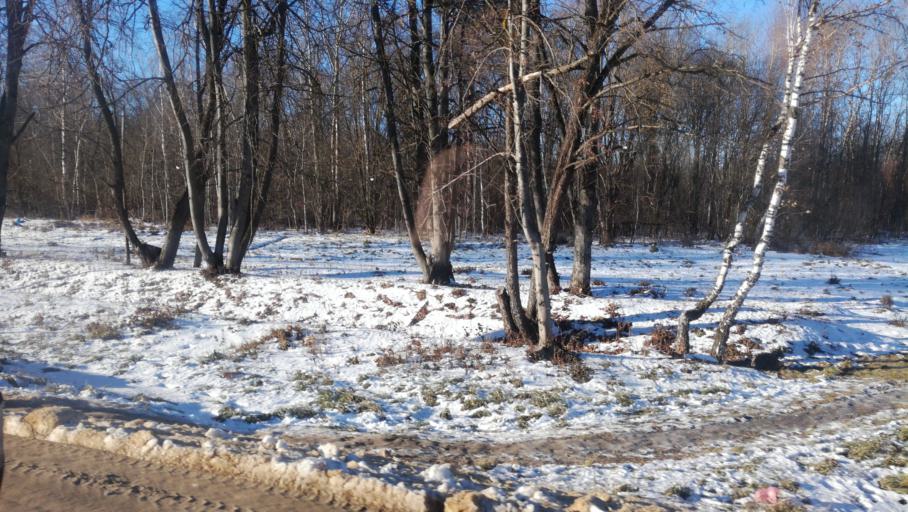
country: RU
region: Tula
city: Kosaya Gora
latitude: 54.1657
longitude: 37.4674
